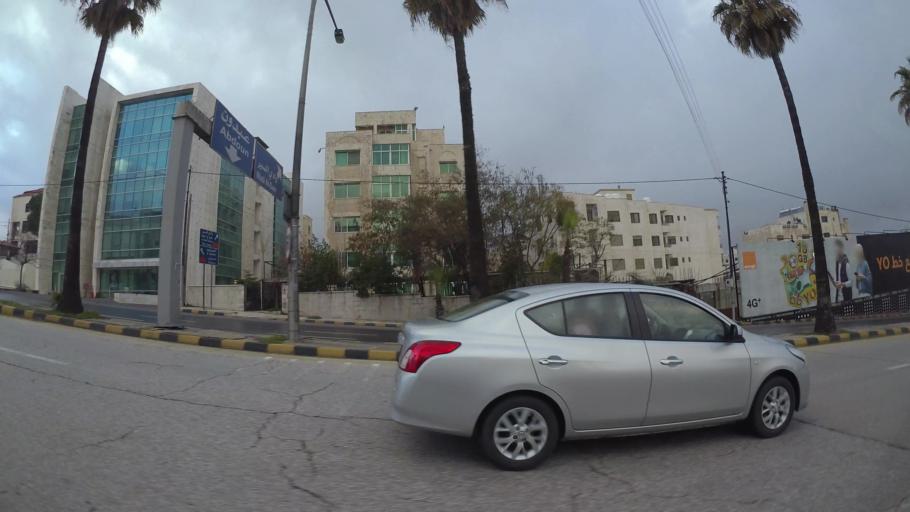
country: JO
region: Amman
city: Amman
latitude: 31.9631
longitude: 35.8831
